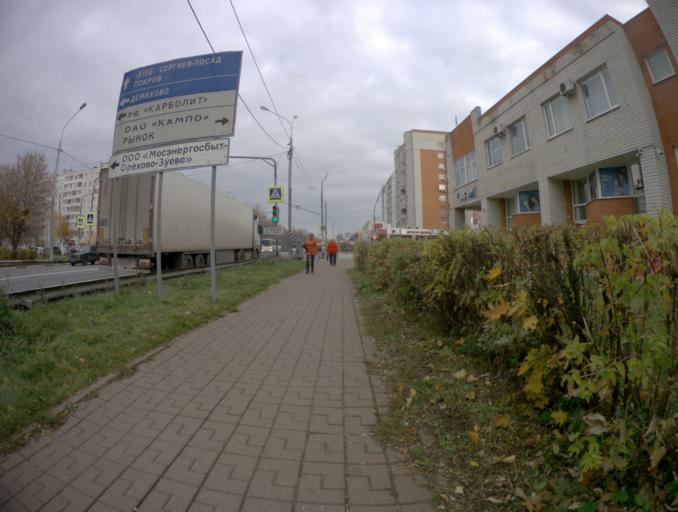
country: RU
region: Moskovskaya
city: Orekhovo-Zuyevo
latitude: 55.8078
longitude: 38.9680
